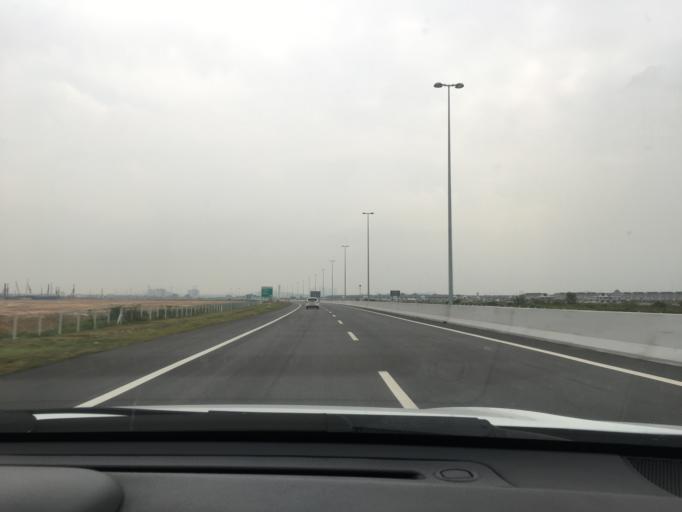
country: MY
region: Selangor
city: Klang
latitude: 3.1007
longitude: 101.4230
